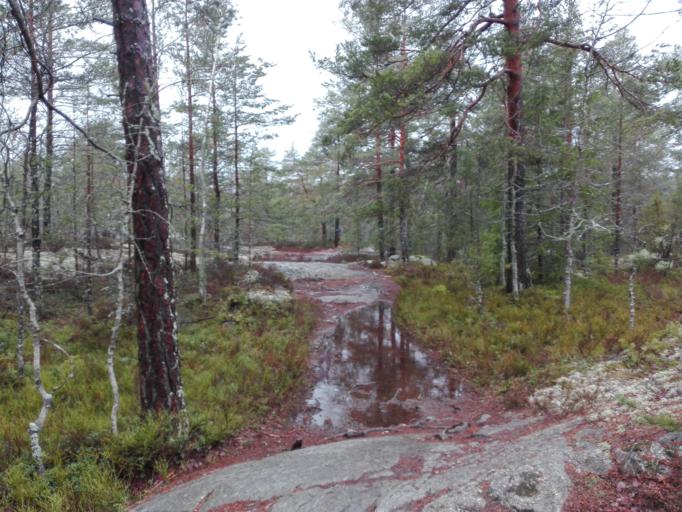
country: SE
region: Stockholm
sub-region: Nacka Kommun
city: Fisksatra
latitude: 59.2750
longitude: 18.2569
